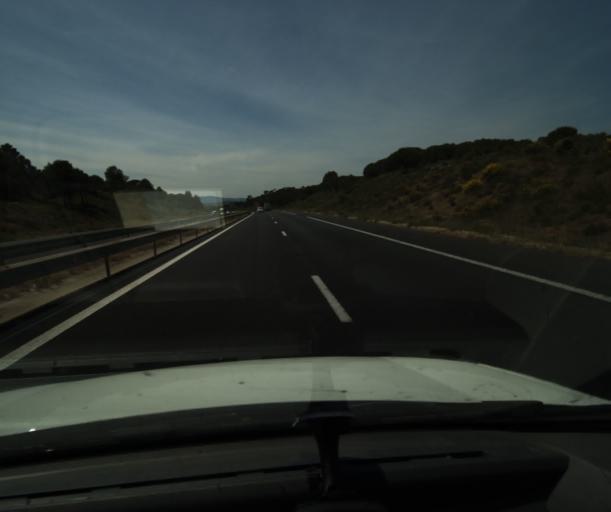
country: FR
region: Languedoc-Roussillon
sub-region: Departement de l'Aude
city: Bizanet
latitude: 43.1565
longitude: 2.8972
